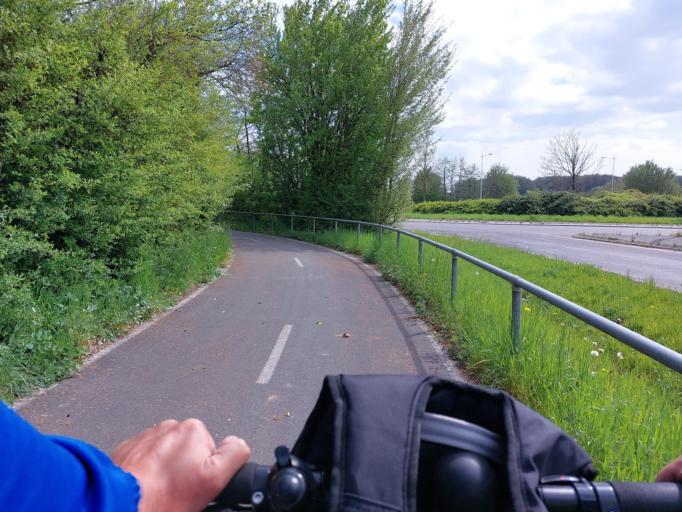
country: FR
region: Nord-Pas-de-Calais
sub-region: Departement du Nord
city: Hautmont
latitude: 50.2625
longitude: 3.8969
